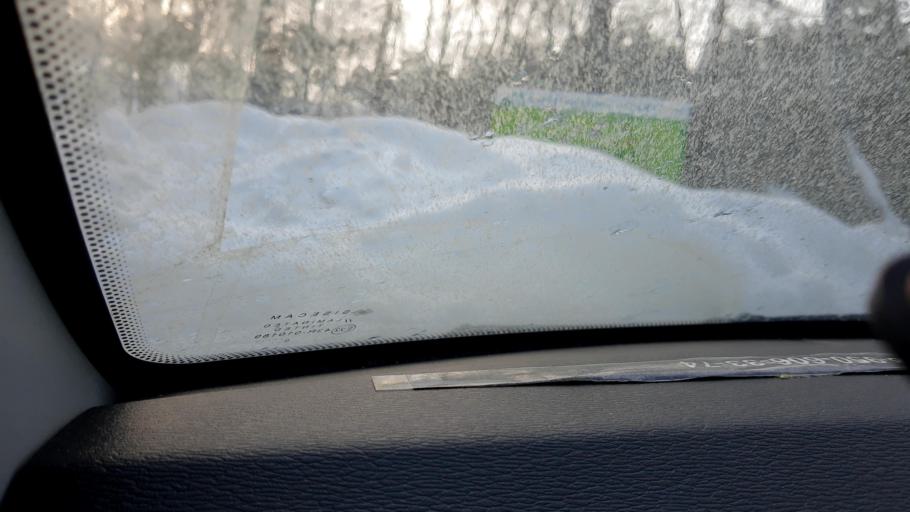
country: RU
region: Nizjnij Novgorod
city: Afonino
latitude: 56.1727
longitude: 44.0762
